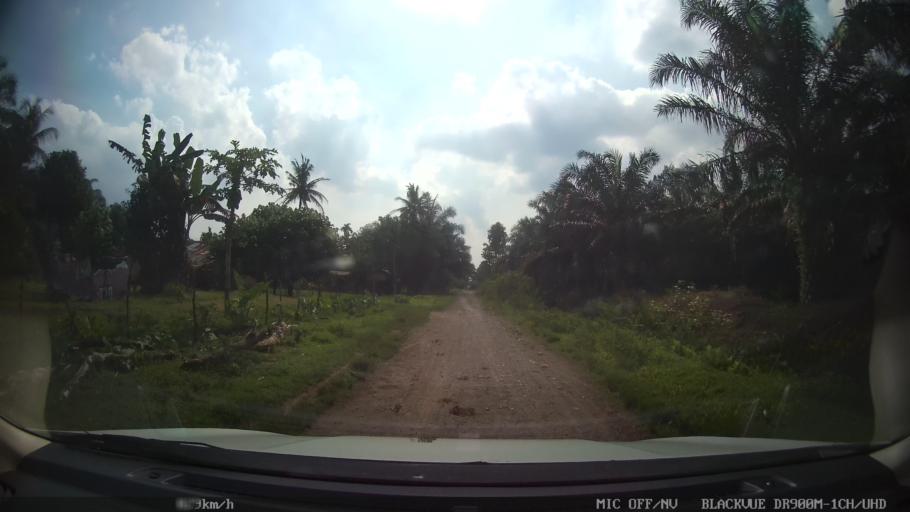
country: ID
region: North Sumatra
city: Binjai
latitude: 3.6429
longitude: 98.5191
